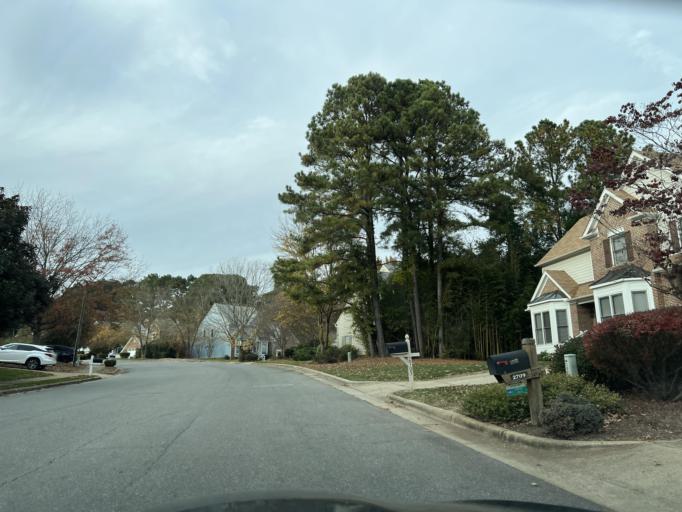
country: US
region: North Carolina
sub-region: Wake County
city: Wake Forest
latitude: 35.8940
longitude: -78.5950
